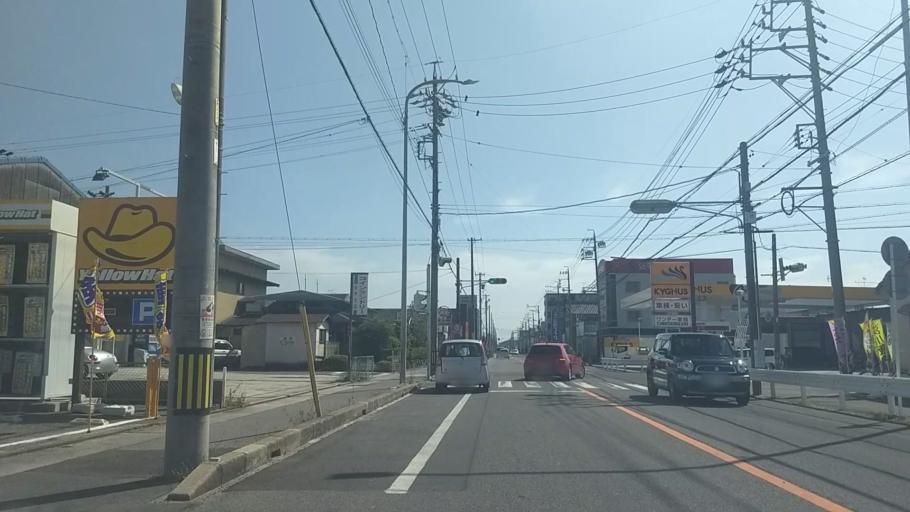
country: JP
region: Aichi
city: Okazaki
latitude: 34.9755
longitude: 137.1356
